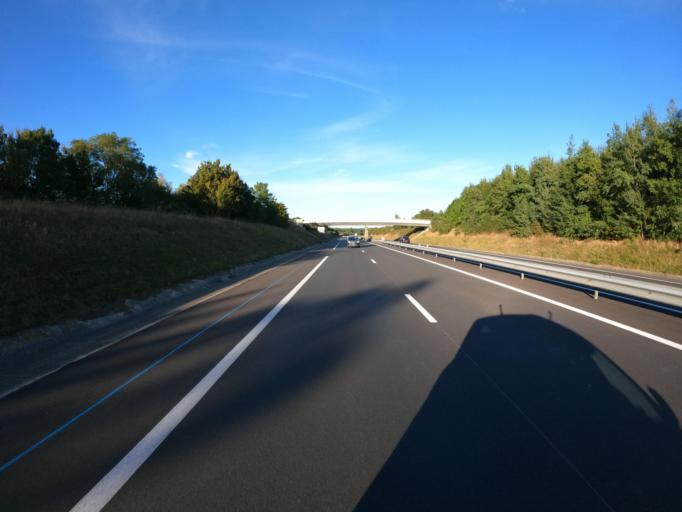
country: FR
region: Pays de la Loire
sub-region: Departement de la Vendee
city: Chambretaud
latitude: 46.9503
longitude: -0.9449
